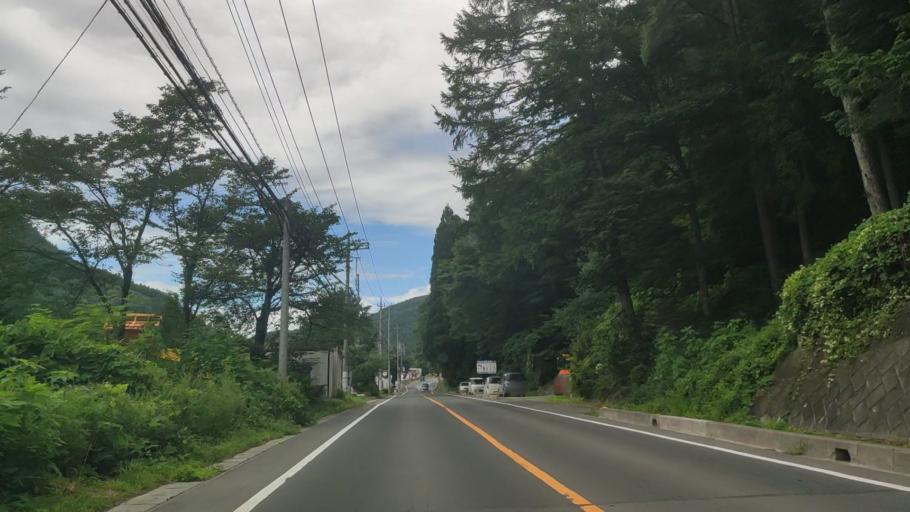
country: JP
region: Gunma
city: Numata
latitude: 36.7389
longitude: 139.2315
